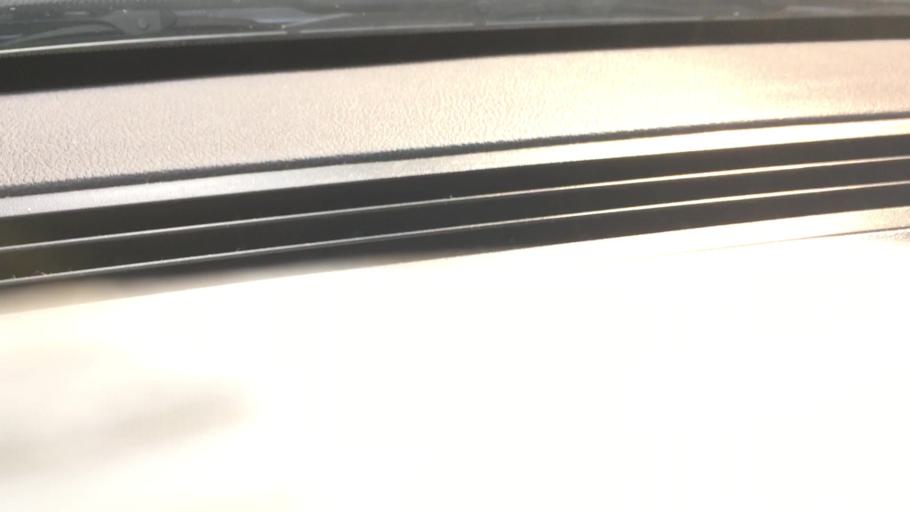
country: US
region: Alabama
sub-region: Shelby County
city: Helena
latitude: 33.2462
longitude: -86.9545
